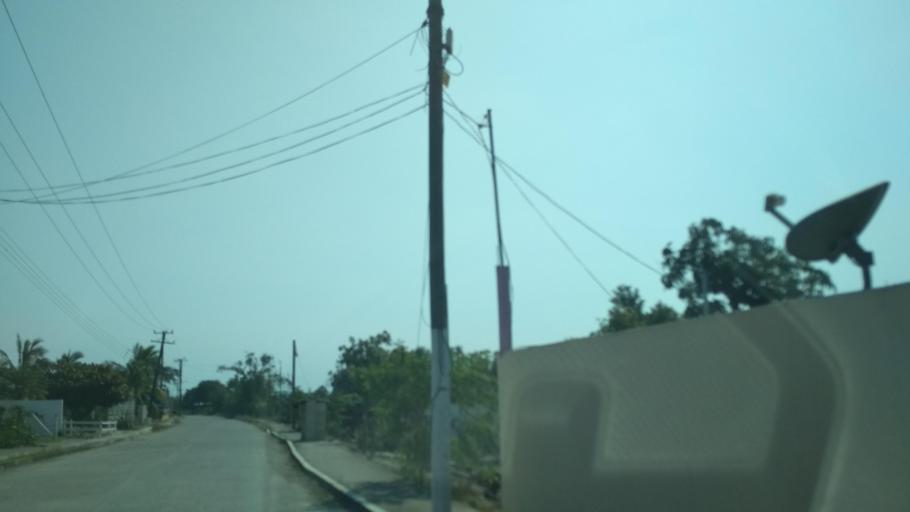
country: MX
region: Veracruz
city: Gutierrez Zamora
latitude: 20.4166
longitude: -97.1874
